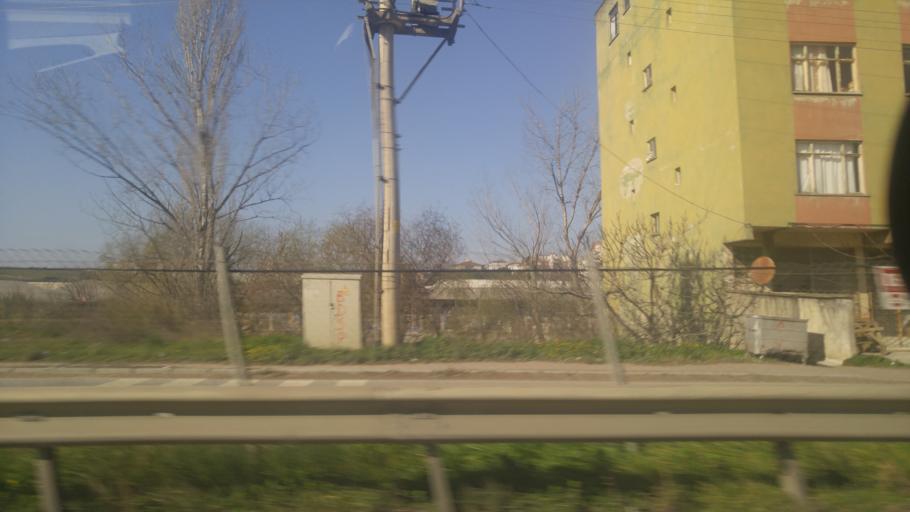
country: TR
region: Kocaeli
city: Darica
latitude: 40.8251
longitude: 29.3649
